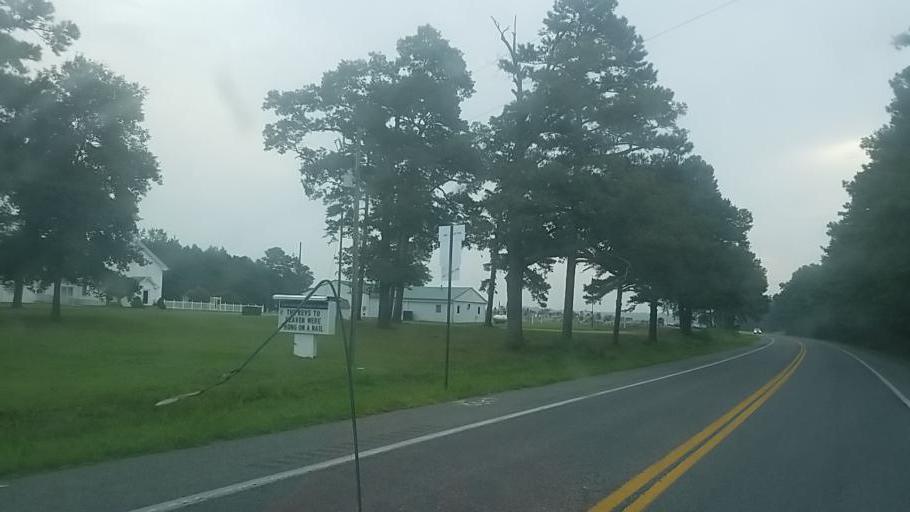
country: US
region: Maryland
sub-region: Wicomico County
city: Pittsville
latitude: 38.4519
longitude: -75.4185
